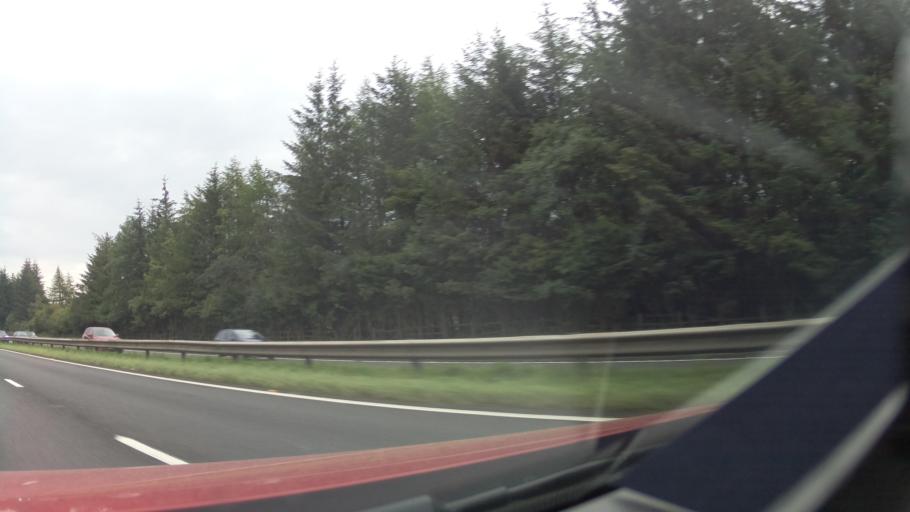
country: GB
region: Scotland
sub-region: North Lanarkshire
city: Caldercruix
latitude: 55.8471
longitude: -3.8620
